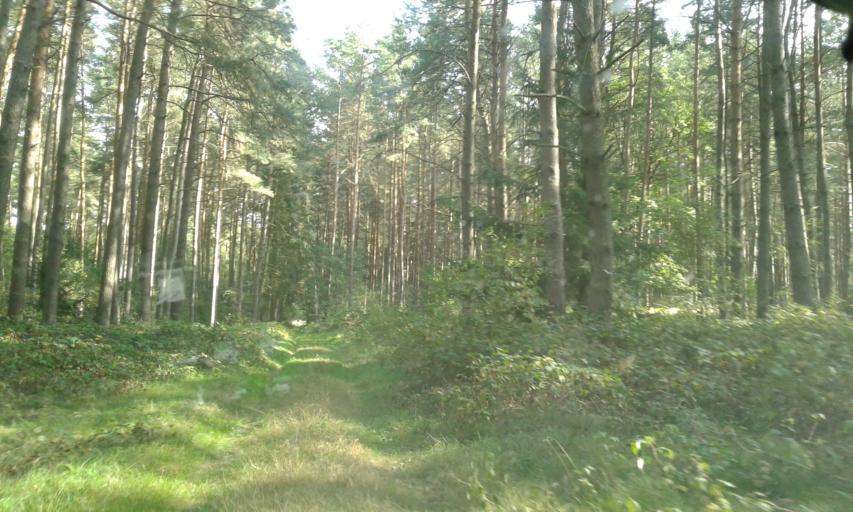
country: PL
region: West Pomeranian Voivodeship
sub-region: Powiat stargardzki
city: Suchan
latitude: 53.2435
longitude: 15.3586
